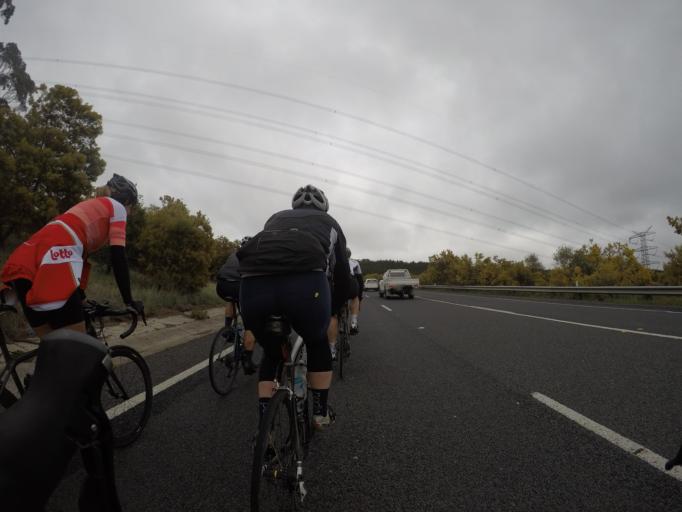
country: AU
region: New South Wales
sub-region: Lithgow
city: Portland
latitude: -33.4555
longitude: 149.9767
